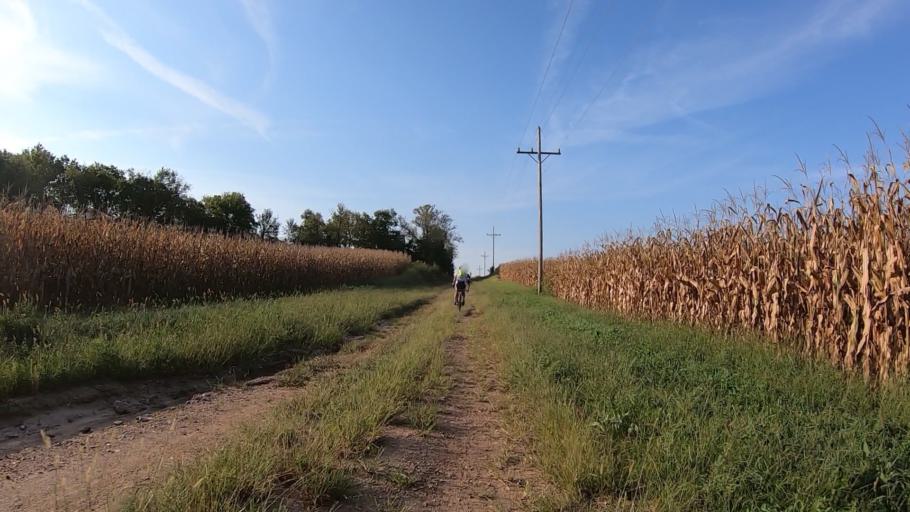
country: US
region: Kansas
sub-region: Marshall County
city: Blue Rapids
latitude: 39.7105
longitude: -96.7793
